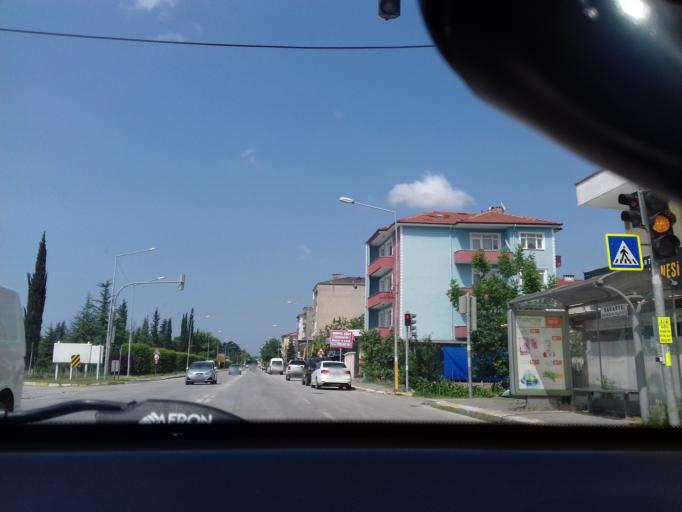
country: TR
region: Sakarya
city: Adapazari
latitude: 40.7251
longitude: 30.3731
